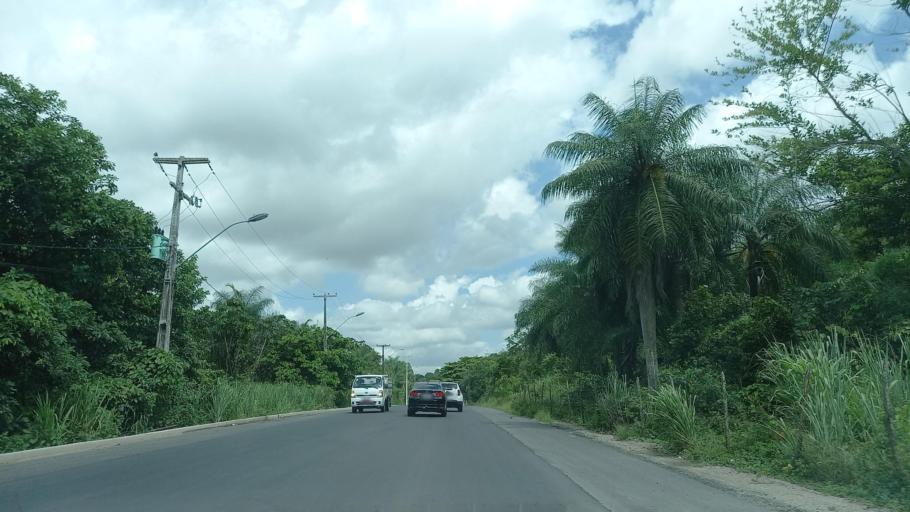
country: BR
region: Pernambuco
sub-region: Jaboatao Dos Guararapes
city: Jaboatao dos Guararapes
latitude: -8.1438
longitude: -35.0006
